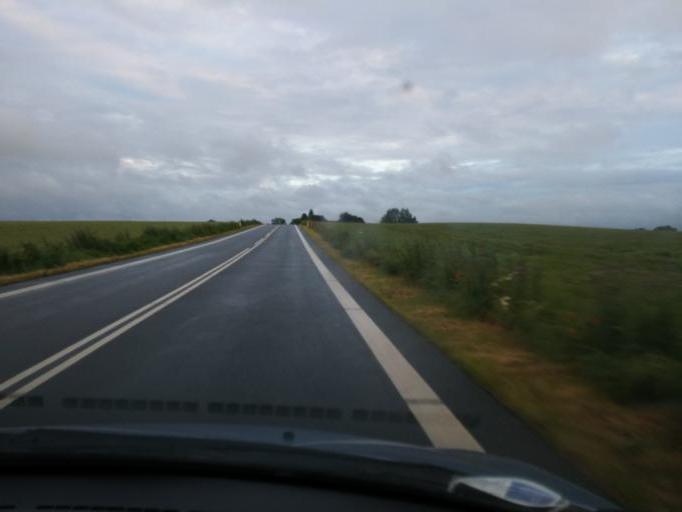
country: DK
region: South Denmark
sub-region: Kerteminde Kommune
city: Kerteminde
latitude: 55.4893
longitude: 10.6580
